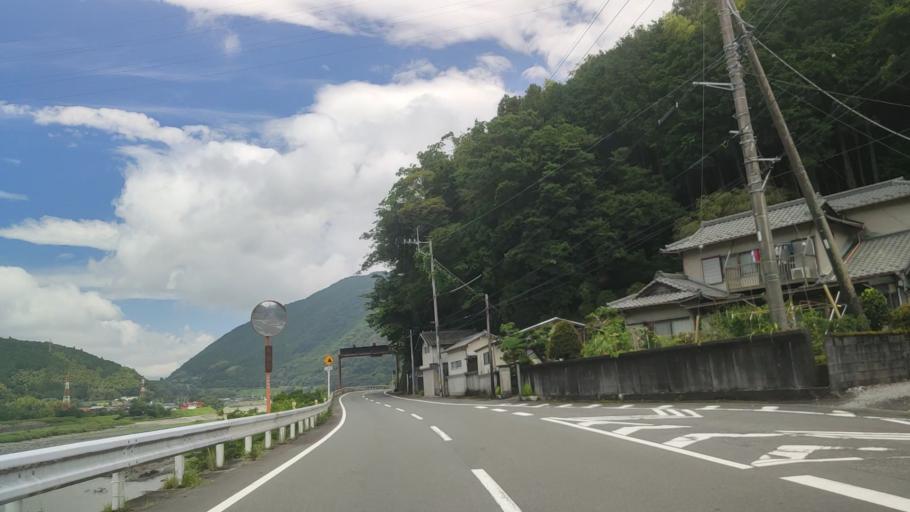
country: JP
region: Shizuoka
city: Fujinomiya
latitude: 35.2319
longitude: 138.5116
